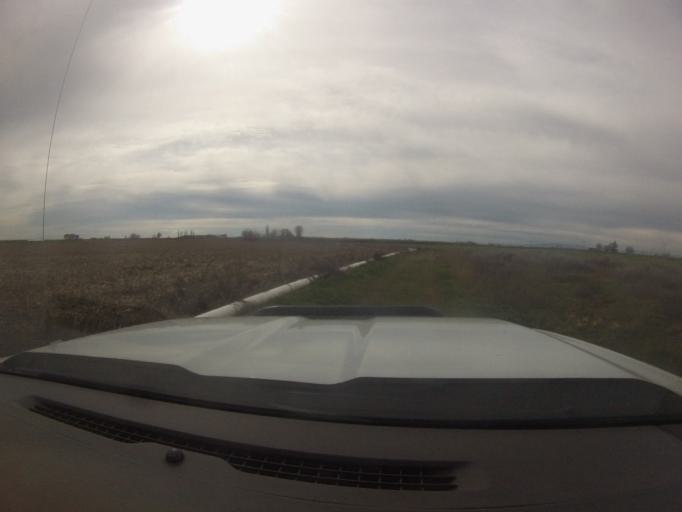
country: US
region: Washington
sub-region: Franklin County
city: Basin City
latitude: 46.6051
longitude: -119.0470
